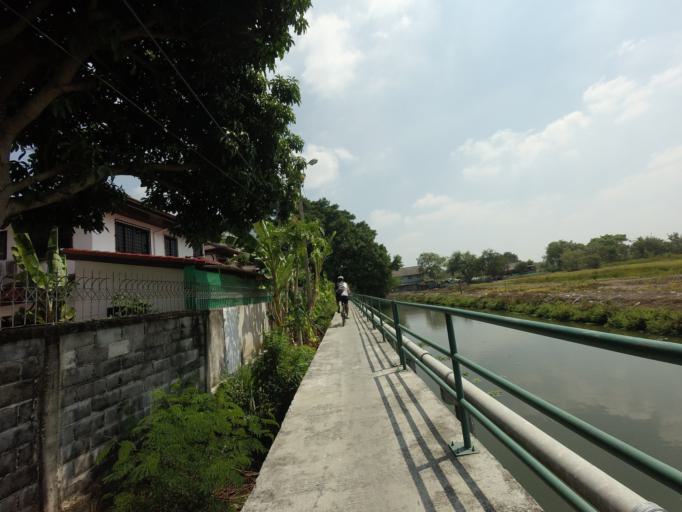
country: TH
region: Bangkok
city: Saphan Sung
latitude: 13.7540
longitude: 100.6744
